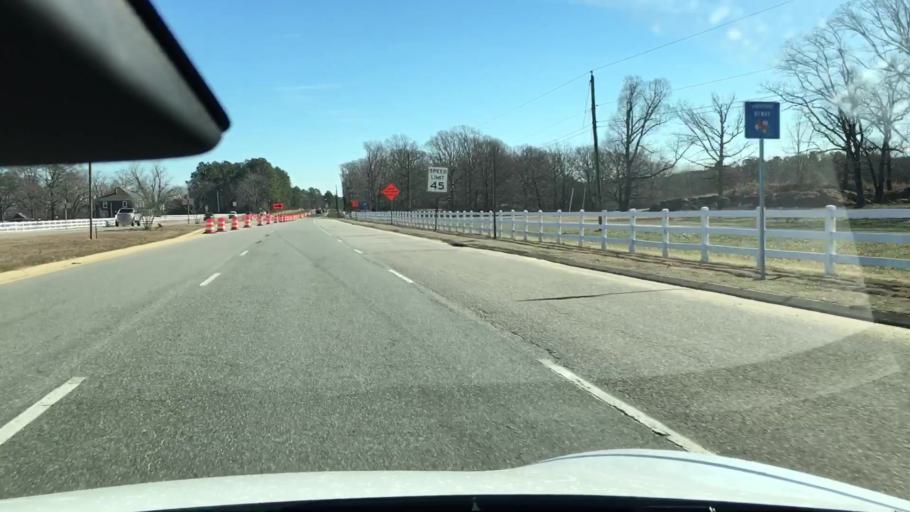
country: US
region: Virginia
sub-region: Henrico County
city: Short Pump
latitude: 37.5587
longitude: -77.6861
